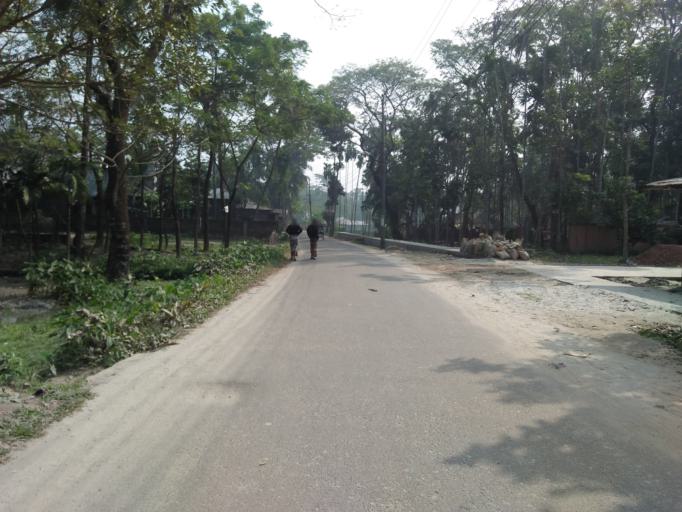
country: BD
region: Barisal
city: Bhola
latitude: 22.6800
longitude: 90.6378
